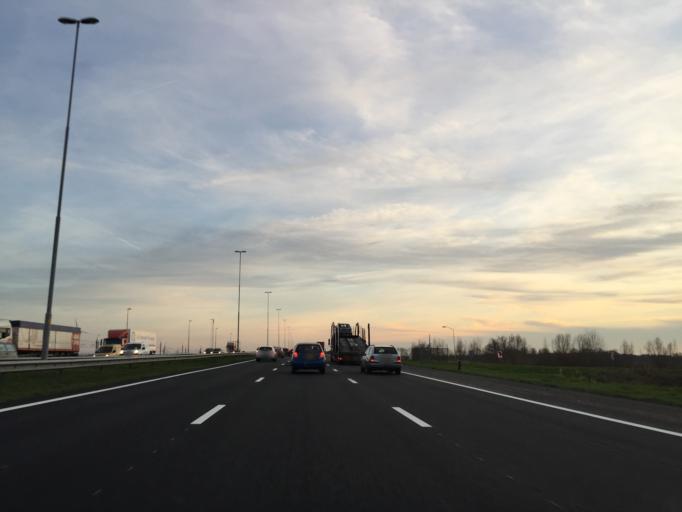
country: NL
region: North Brabant
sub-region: Gemeente Breda
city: Breda
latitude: 51.6410
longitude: 4.6953
